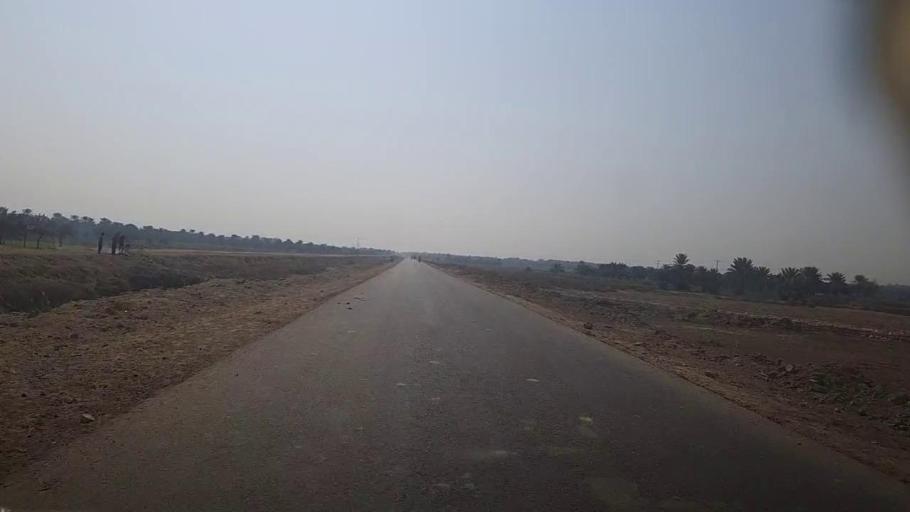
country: PK
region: Sindh
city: Khairpur
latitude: 27.4764
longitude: 68.8243
